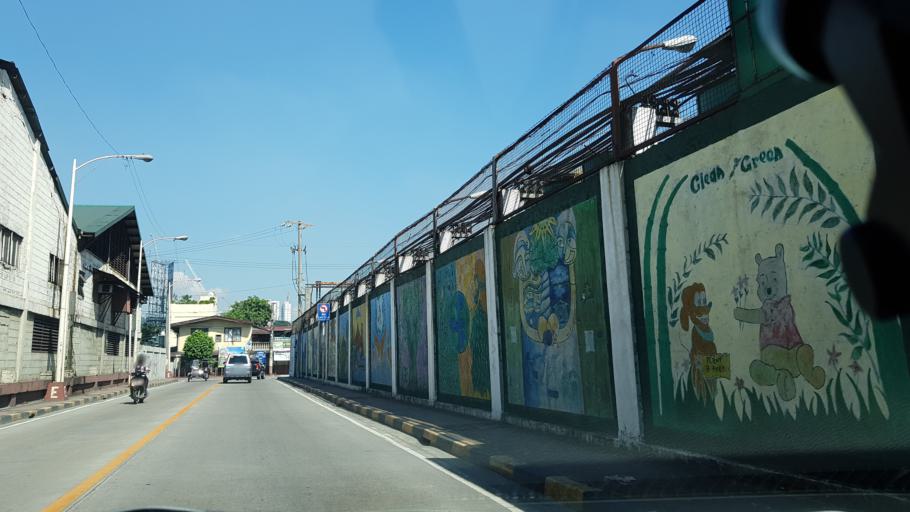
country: PH
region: Calabarzon
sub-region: Province of Rizal
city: Pateros
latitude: 14.5611
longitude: 121.0712
